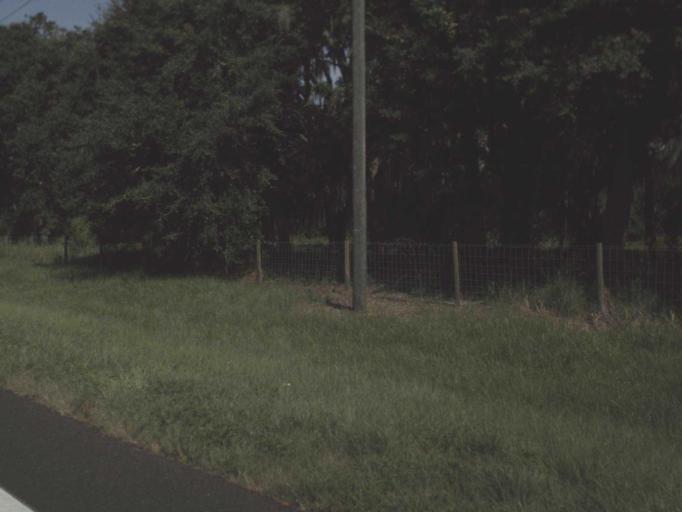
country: US
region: Florida
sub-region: Hillsborough County
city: Plant City
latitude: 27.9379
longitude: -82.1007
